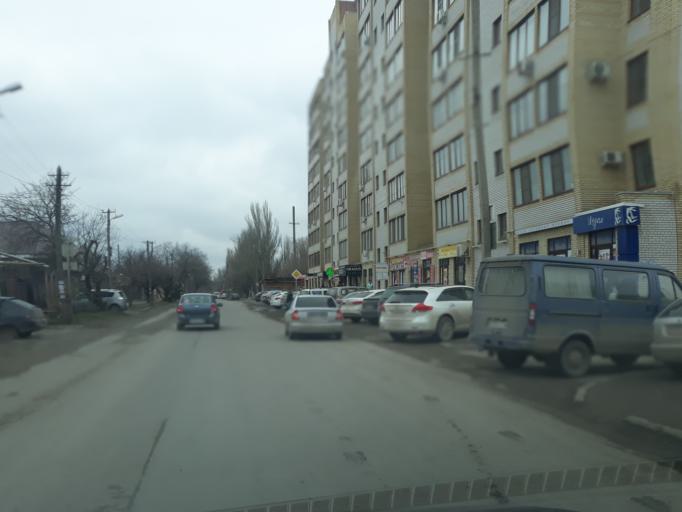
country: RU
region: Rostov
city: Taganrog
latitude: 47.2628
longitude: 38.9115
